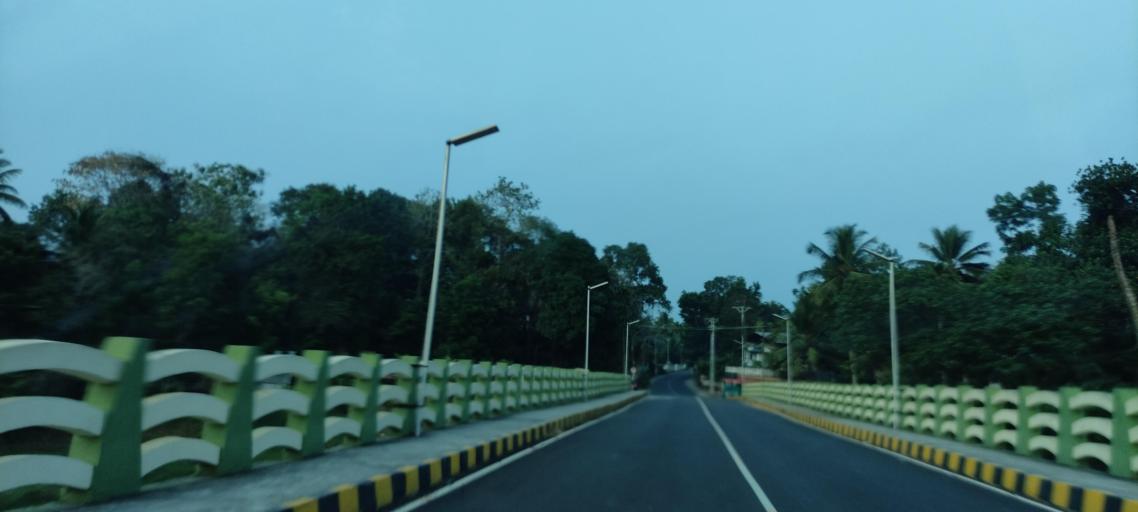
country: IN
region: Kerala
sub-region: Alappuzha
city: Mavelikara
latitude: 9.2709
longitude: 76.5571
